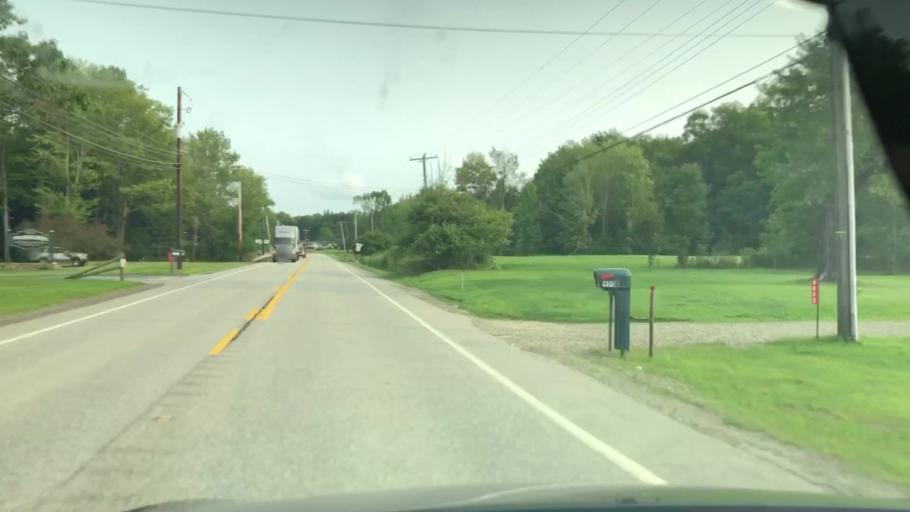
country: US
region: Pennsylvania
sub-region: Erie County
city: Wesleyville
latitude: 42.0709
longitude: -79.9829
